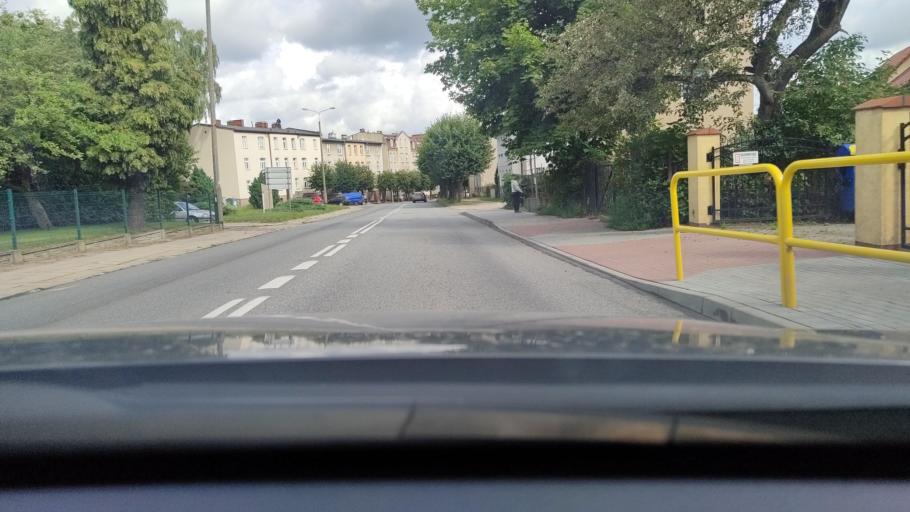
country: PL
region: Pomeranian Voivodeship
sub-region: Powiat wejherowski
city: Wejherowo
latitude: 54.5972
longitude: 18.2323
